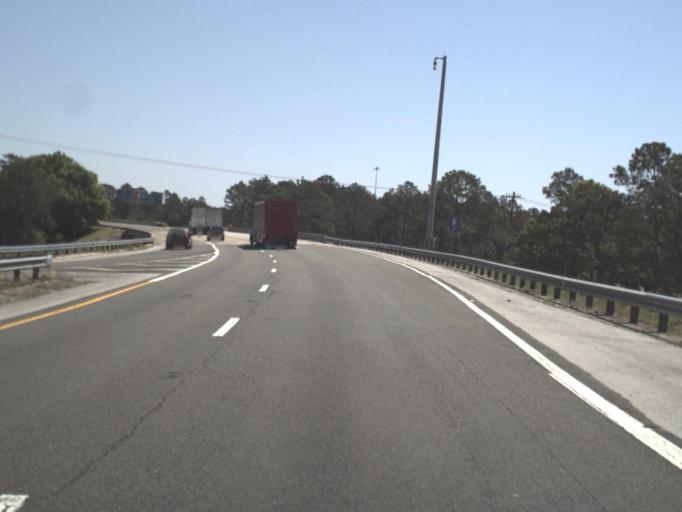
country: US
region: Florida
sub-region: Escambia County
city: Ensley
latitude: 30.5024
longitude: -87.2674
